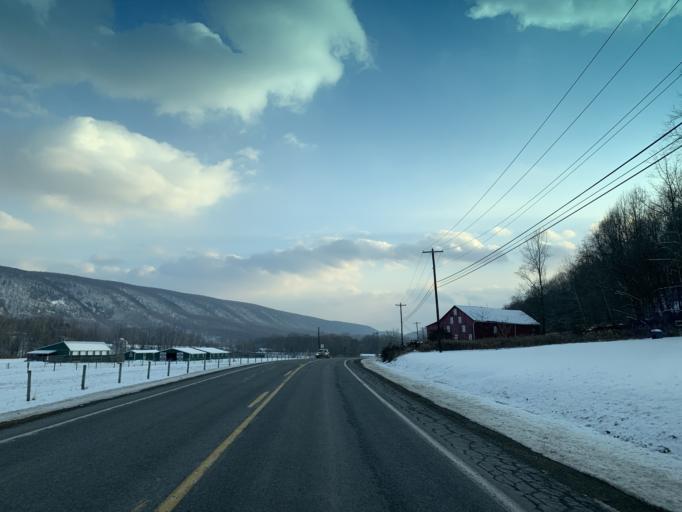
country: US
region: Maryland
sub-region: Allegany County
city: Cumberland
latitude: 39.7550
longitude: -78.7493
